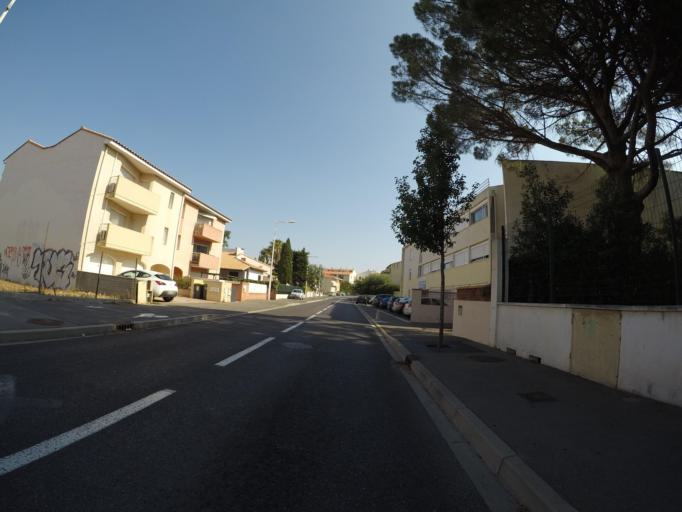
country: FR
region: Languedoc-Roussillon
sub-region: Departement des Pyrenees-Orientales
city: Perpignan
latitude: 42.6853
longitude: 2.8988
